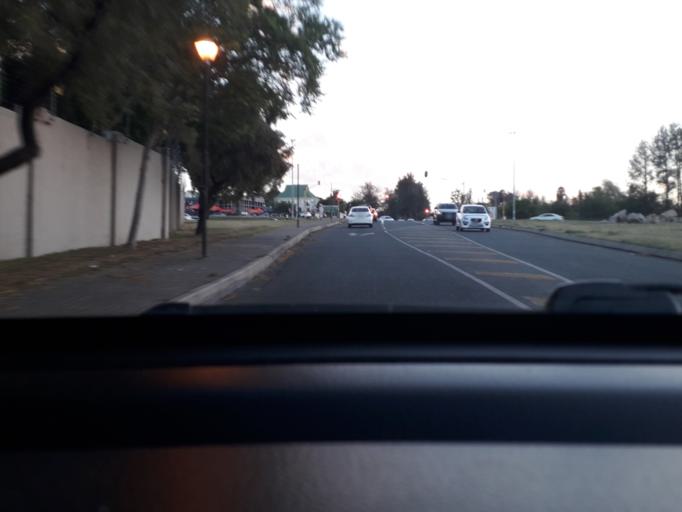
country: ZA
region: Gauteng
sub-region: City of Johannesburg Metropolitan Municipality
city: Diepsloot
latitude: -26.0245
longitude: 28.0213
